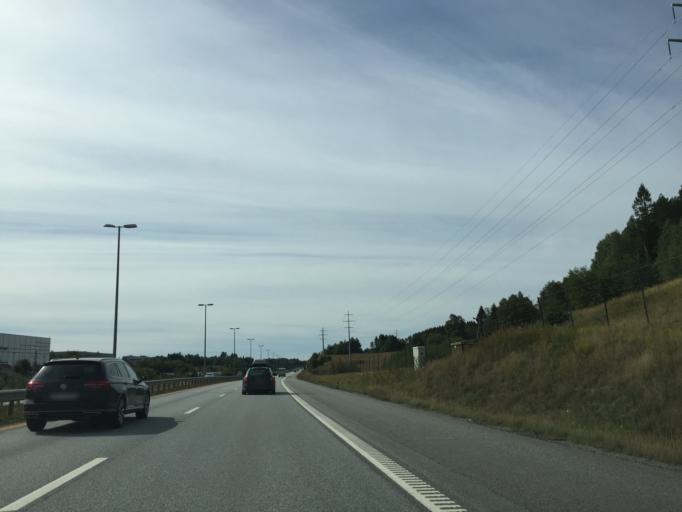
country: NO
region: Akershus
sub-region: Vestby
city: Vestby
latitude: 59.5917
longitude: 10.7381
